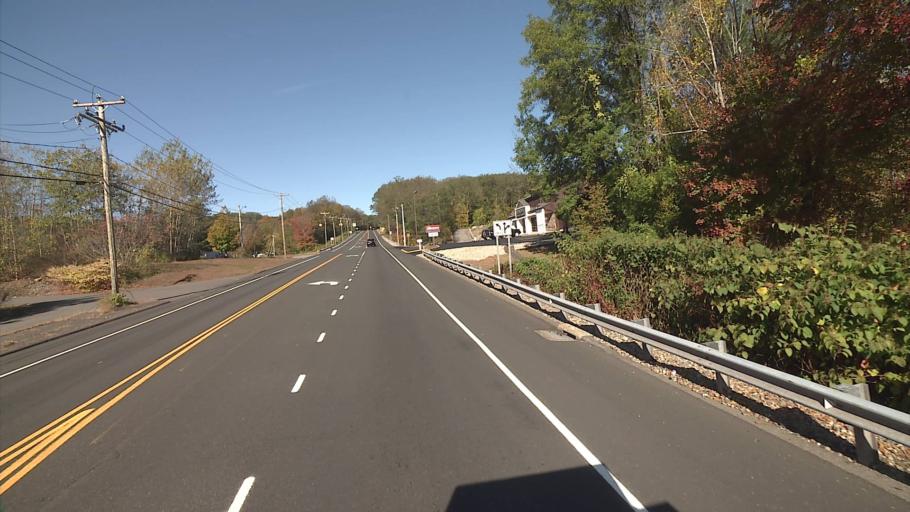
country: US
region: Connecticut
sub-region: Tolland County
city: Rockville
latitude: 41.7854
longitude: -72.4376
